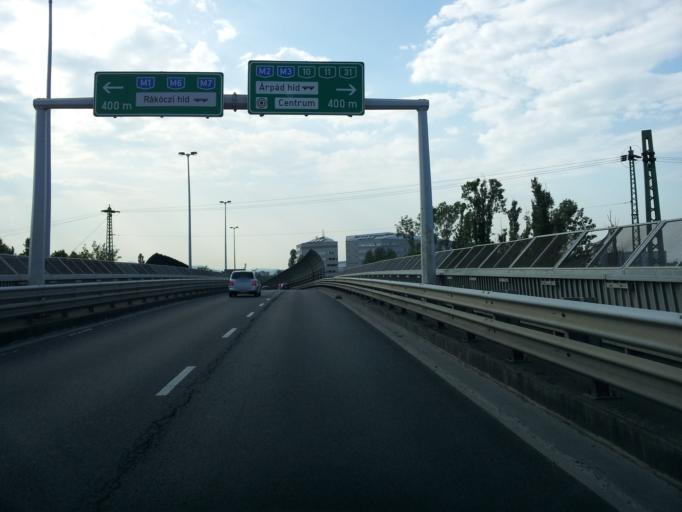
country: HU
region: Budapest
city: Budapest XX. keruelet
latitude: 47.4707
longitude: 19.1009
